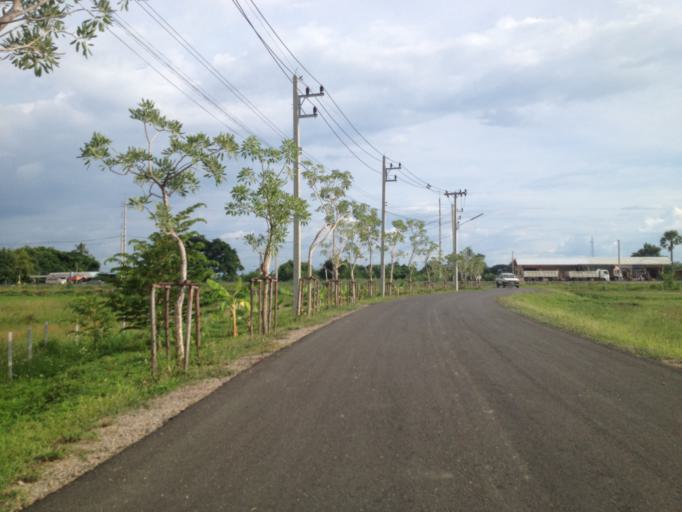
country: TH
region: Chiang Mai
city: Hang Dong
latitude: 18.7097
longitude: 98.9174
